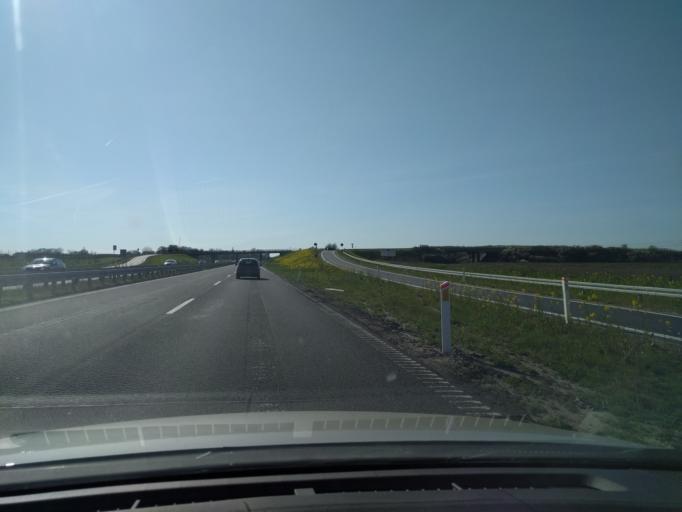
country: DK
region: Zealand
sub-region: Slagelse Kommune
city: Forlev
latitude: 55.3611
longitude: 11.2366
